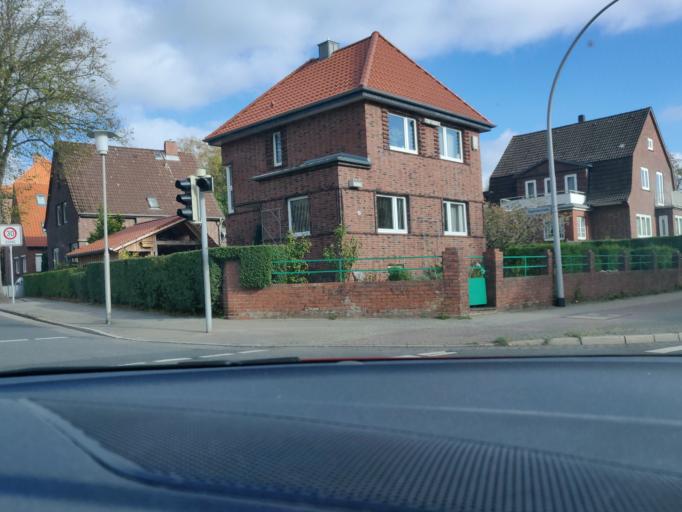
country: DE
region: Lower Saxony
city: Cuxhaven
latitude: 53.8589
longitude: 8.6953
